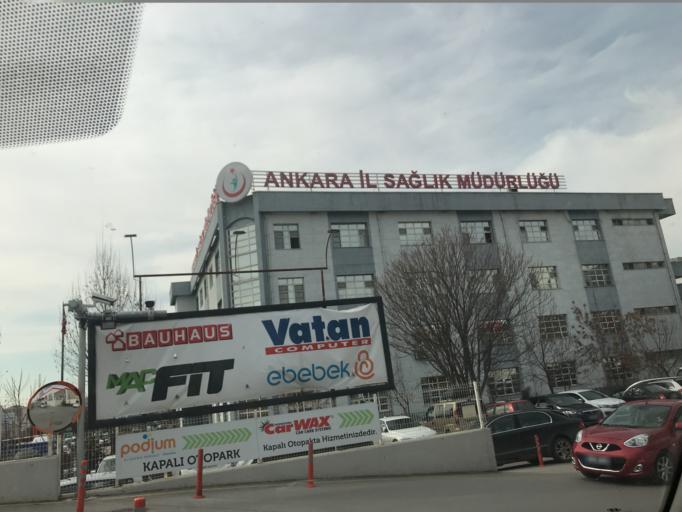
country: TR
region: Ankara
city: Batikent
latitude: 39.9620
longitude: 32.7678
